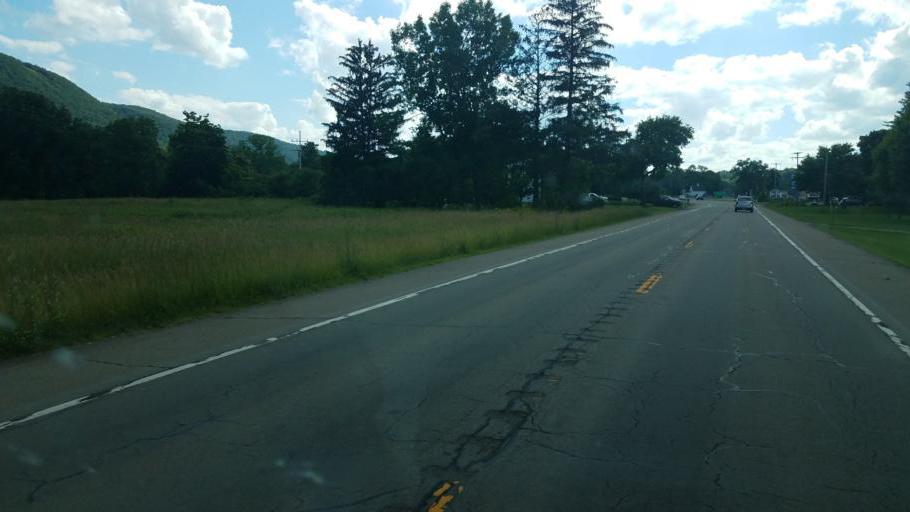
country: US
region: New York
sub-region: Steuben County
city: Bath
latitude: 42.3901
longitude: -77.2560
